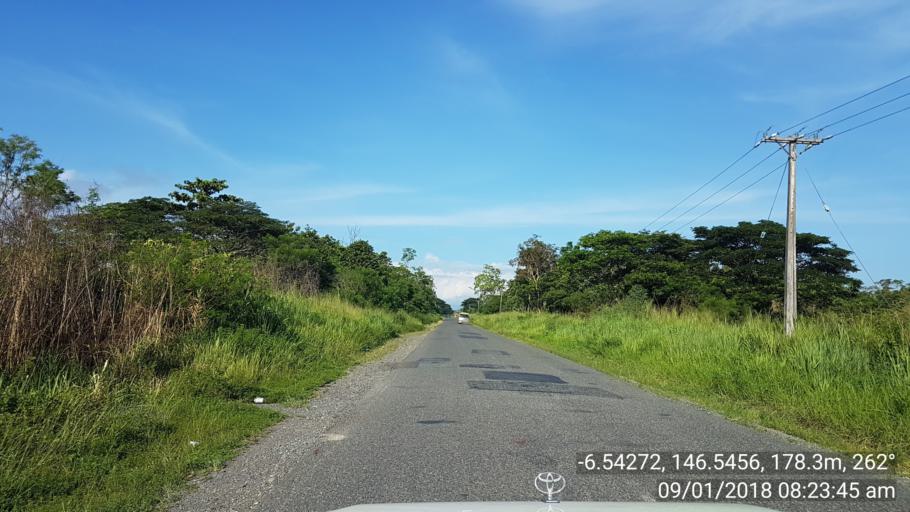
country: PG
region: Morobe
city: Lae
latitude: -6.5429
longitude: 146.5454
